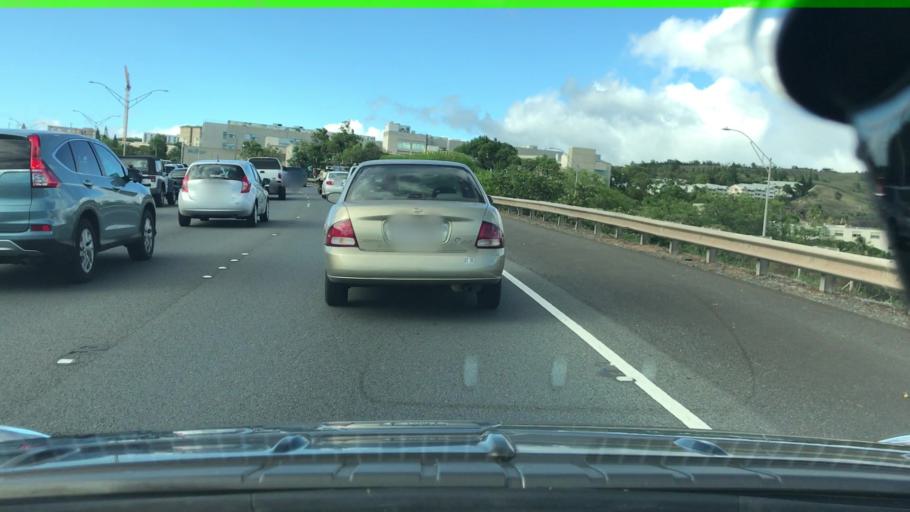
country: US
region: Hawaii
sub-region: Honolulu County
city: Halawa Heights
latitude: 21.3605
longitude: -157.8995
